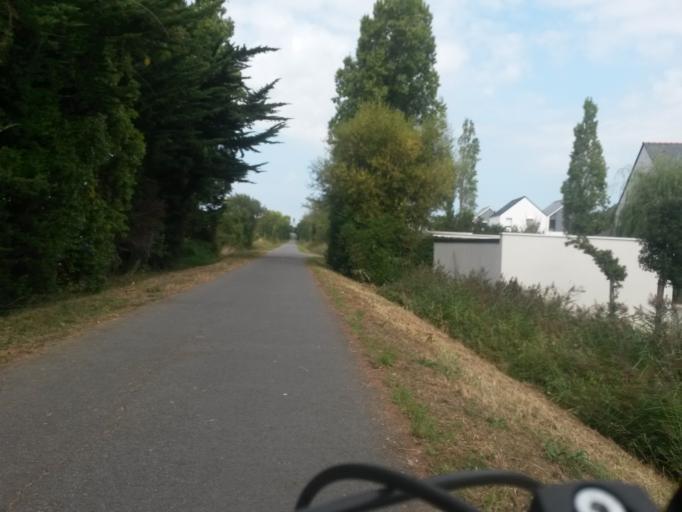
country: FR
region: Pays de la Loire
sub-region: Departement de la Loire-Atlantique
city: La Baule-Escoublac
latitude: 47.2921
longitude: -2.3948
